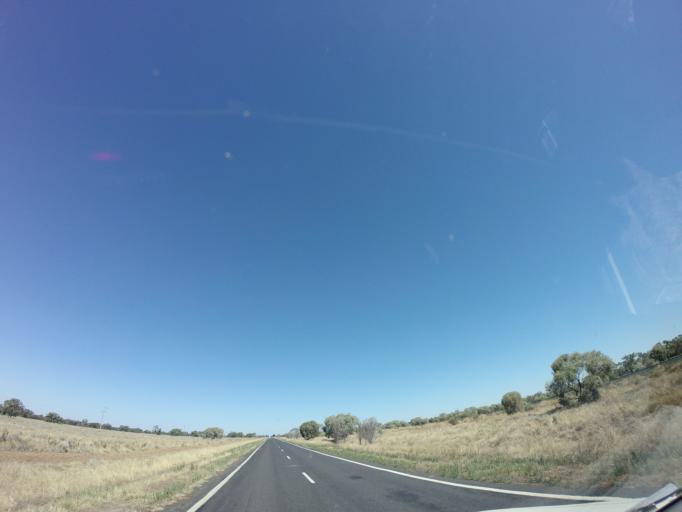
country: AU
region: New South Wales
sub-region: Bogan
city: Nyngan
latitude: -31.6236
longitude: 147.3133
